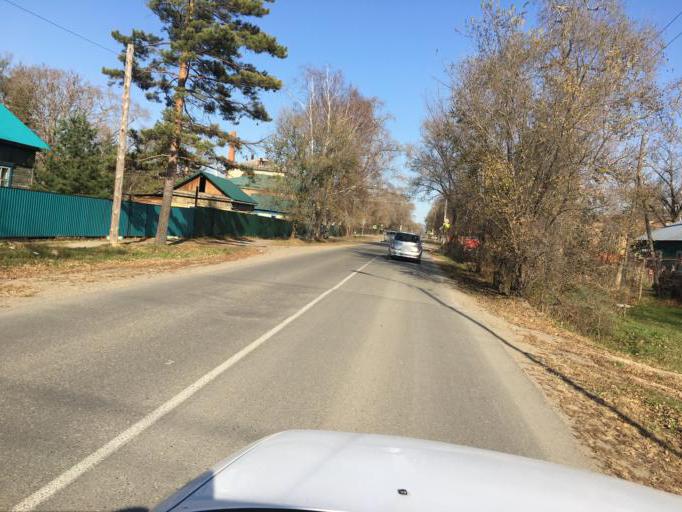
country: RU
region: Primorskiy
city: Dal'nerechensk
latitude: 45.9270
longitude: 133.7307
